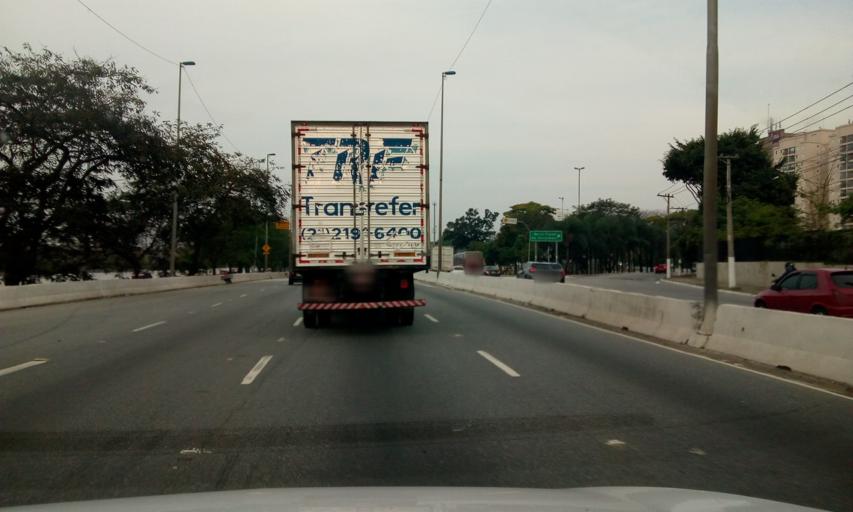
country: BR
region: Sao Paulo
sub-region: Sao Paulo
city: Sao Paulo
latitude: -23.5172
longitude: -46.6573
